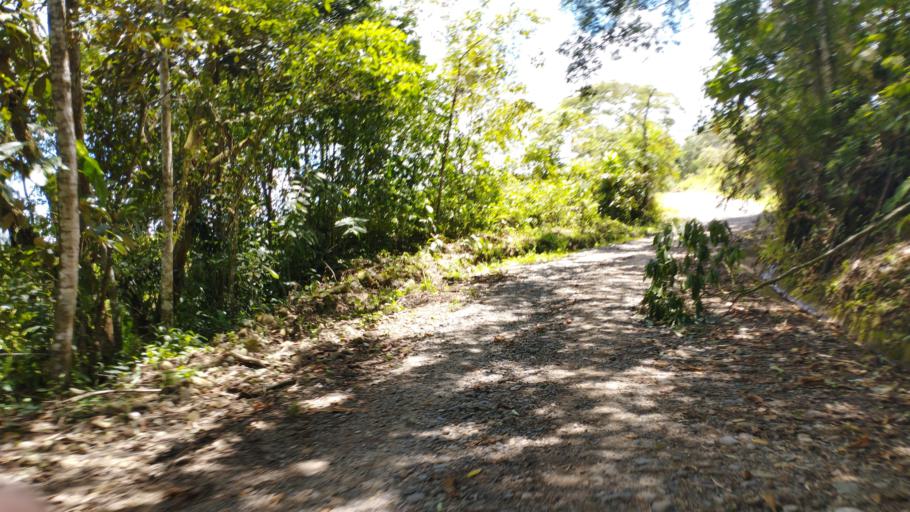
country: CO
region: Boyaca
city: San Luis de Gaceno
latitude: 4.7723
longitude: -73.1359
